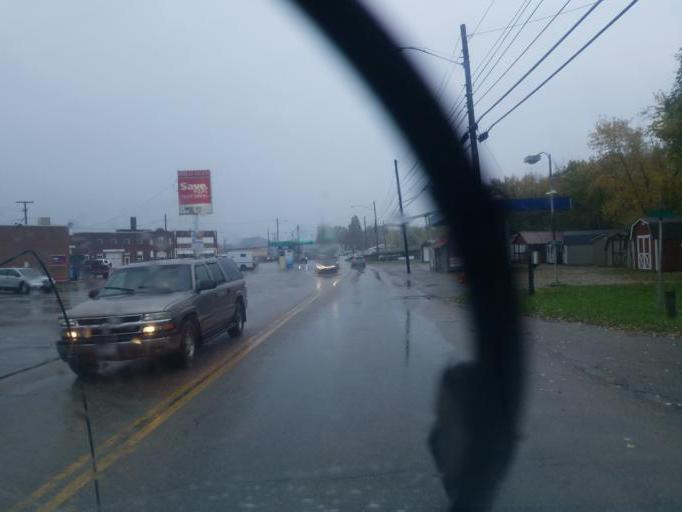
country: US
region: Ohio
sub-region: Morgan County
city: McConnelsville
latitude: 39.6497
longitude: -81.8581
